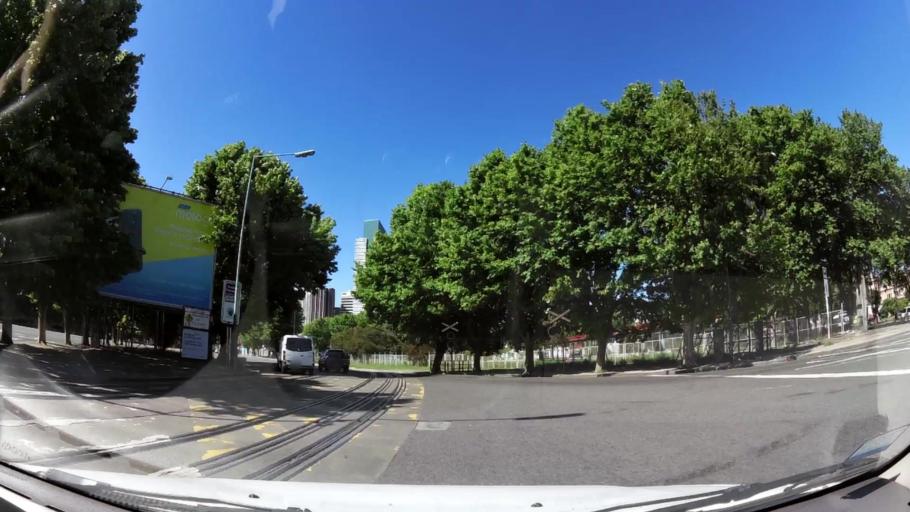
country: AR
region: Buenos Aires F.D.
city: Retiro
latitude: -34.5907
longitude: -58.3707
